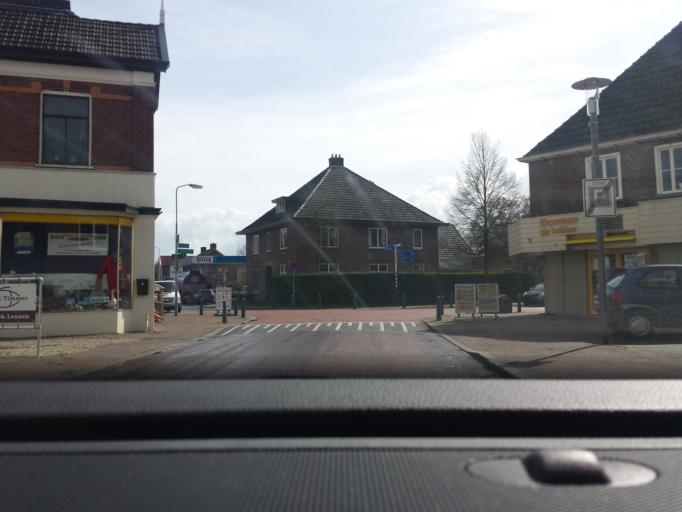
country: NL
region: Gelderland
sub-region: Oude IJsselstreek
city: Varsseveld
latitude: 51.9430
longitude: 6.4640
